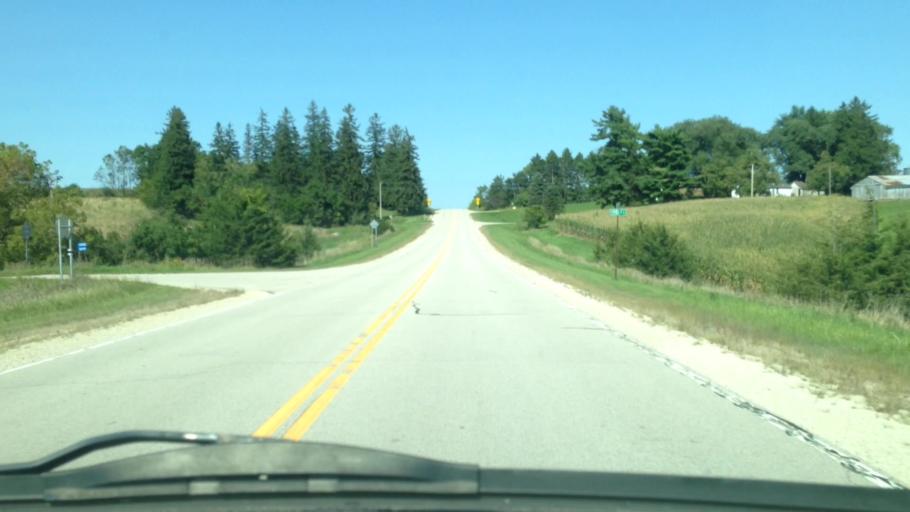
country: US
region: Minnesota
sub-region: Fillmore County
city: Rushford
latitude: 43.6427
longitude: -91.7895
